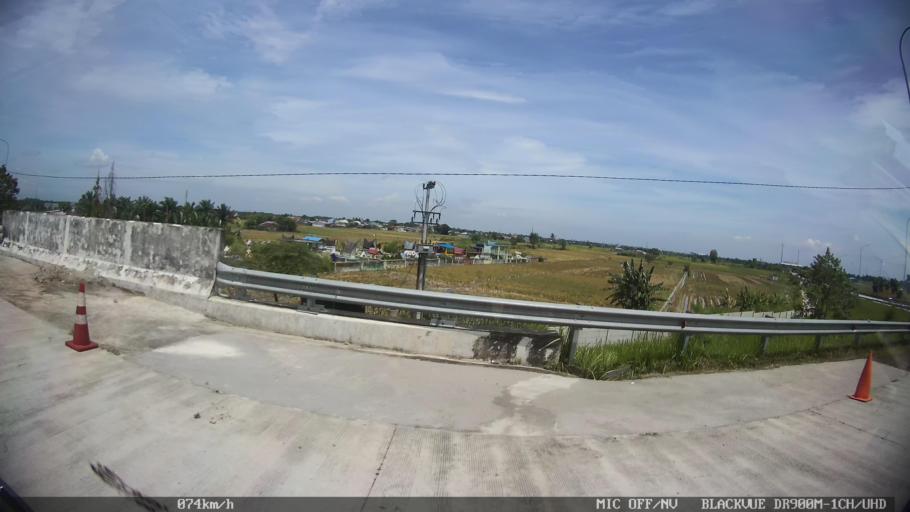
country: ID
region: North Sumatra
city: Perbaungan
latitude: 3.5343
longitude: 98.8926
